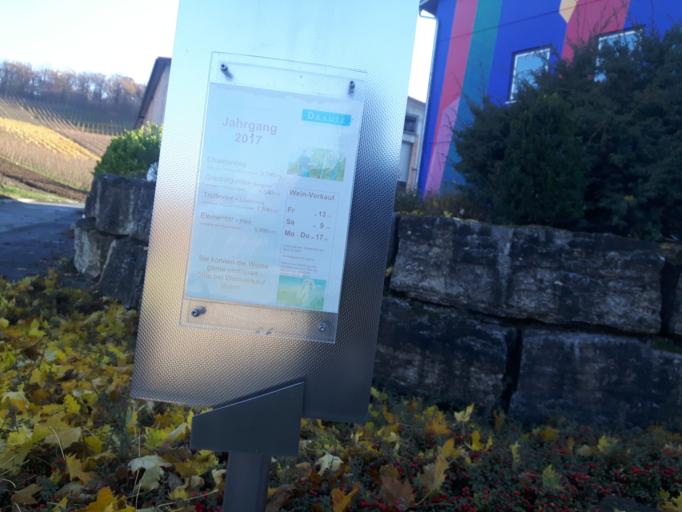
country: DE
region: Baden-Wuerttemberg
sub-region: Regierungsbezirk Stuttgart
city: Heilbronn
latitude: 49.1246
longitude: 9.2395
